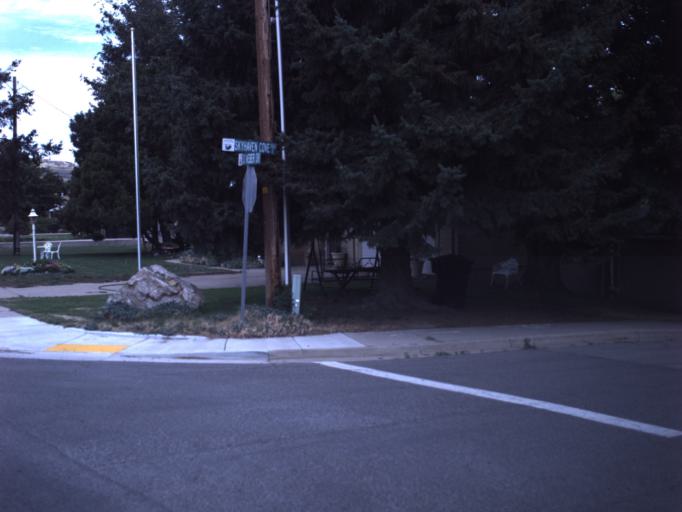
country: US
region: Utah
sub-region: Davis County
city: South Weber
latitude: 41.1343
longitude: -111.9530
